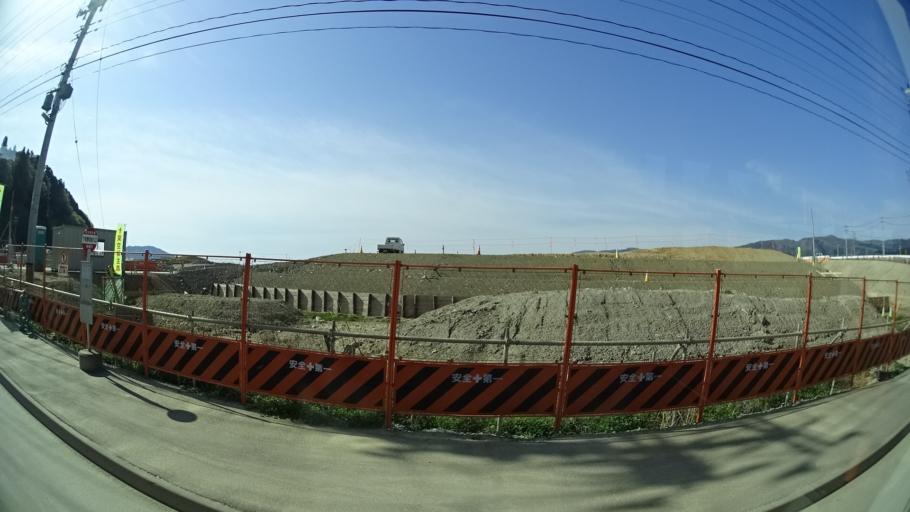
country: JP
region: Iwate
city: Ofunato
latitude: 39.0178
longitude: 141.6327
